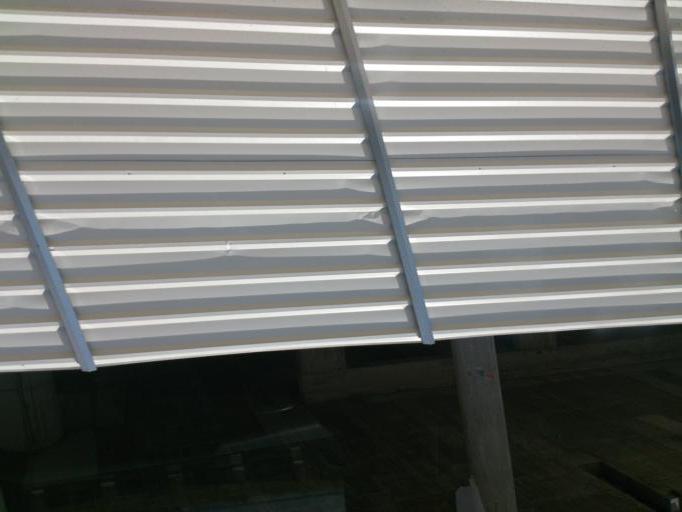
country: PT
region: Lisbon
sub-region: Loures
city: Moscavide
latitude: 38.7455
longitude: -9.0977
